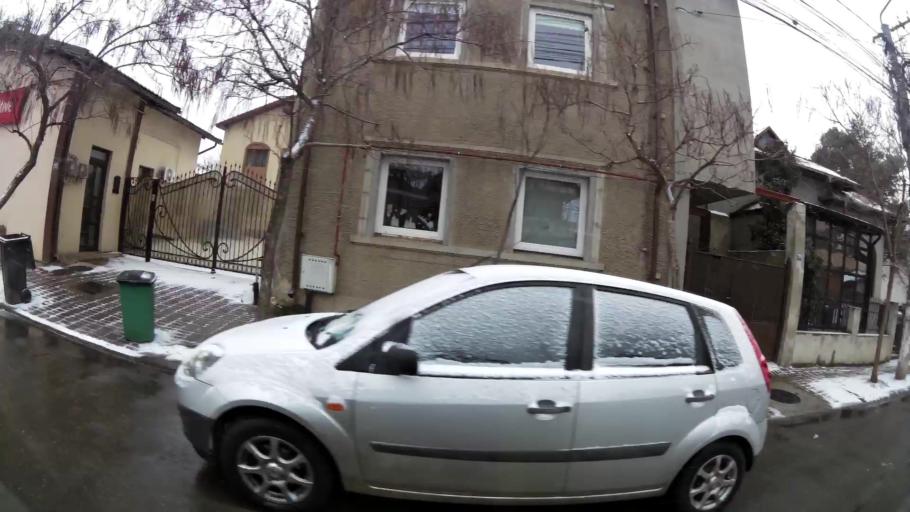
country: RO
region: Dambovita
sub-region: Municipiul Targoviste
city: Targoviste
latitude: 44.9250
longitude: 25.4700
